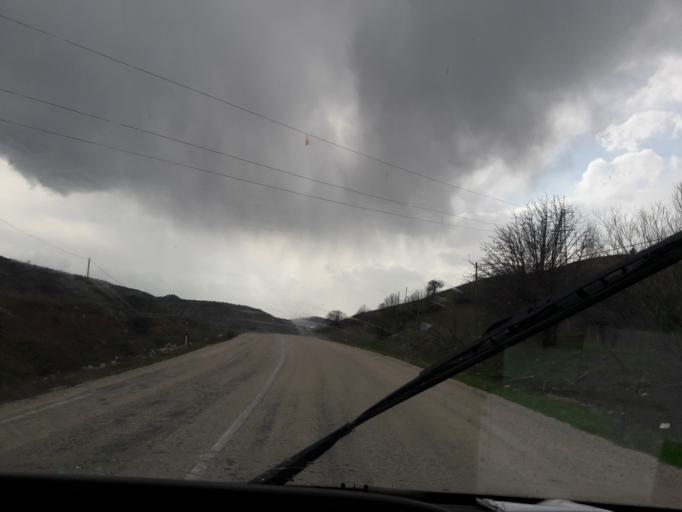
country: TR
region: Giresun
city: Alucra
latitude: 40.2981
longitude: 38.8014
